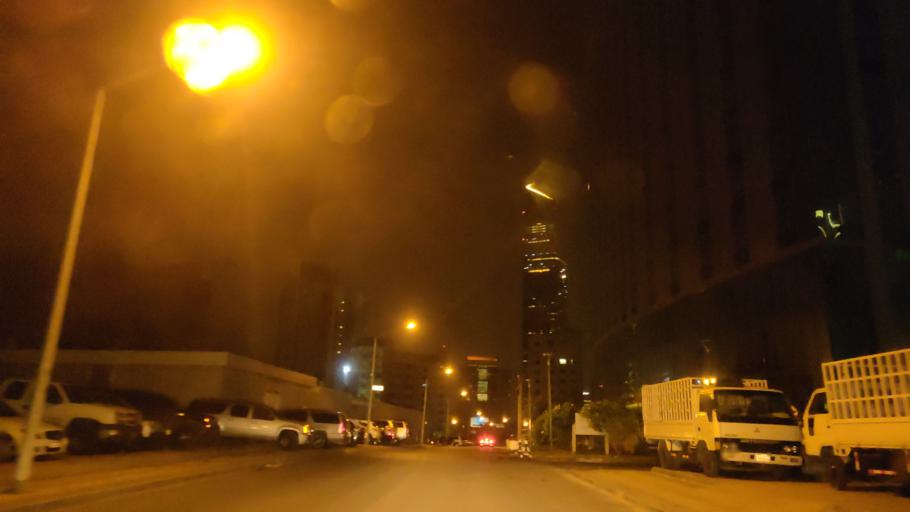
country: KW
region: Al Asimah
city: Kuwait City
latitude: 29.3890
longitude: 47.9909
